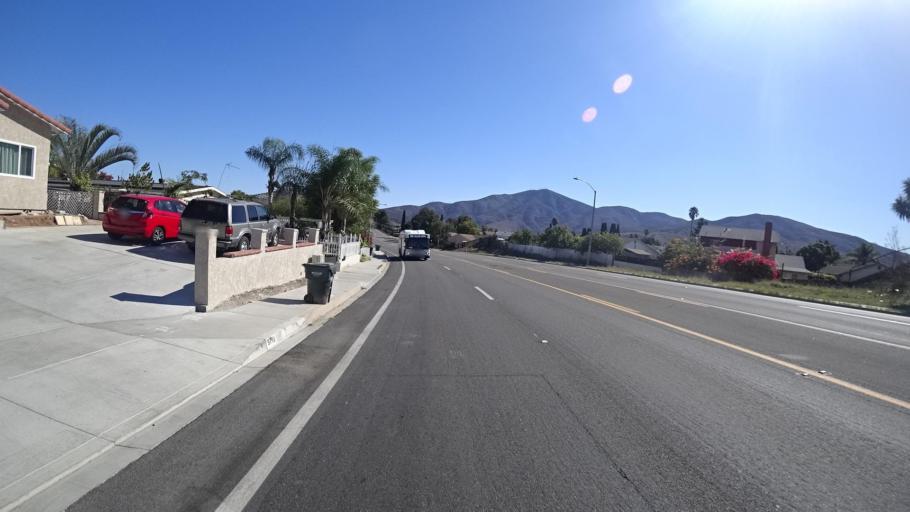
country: US
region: California
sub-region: San Diego County
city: La Presa
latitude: 32.7079
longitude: -116.9893
